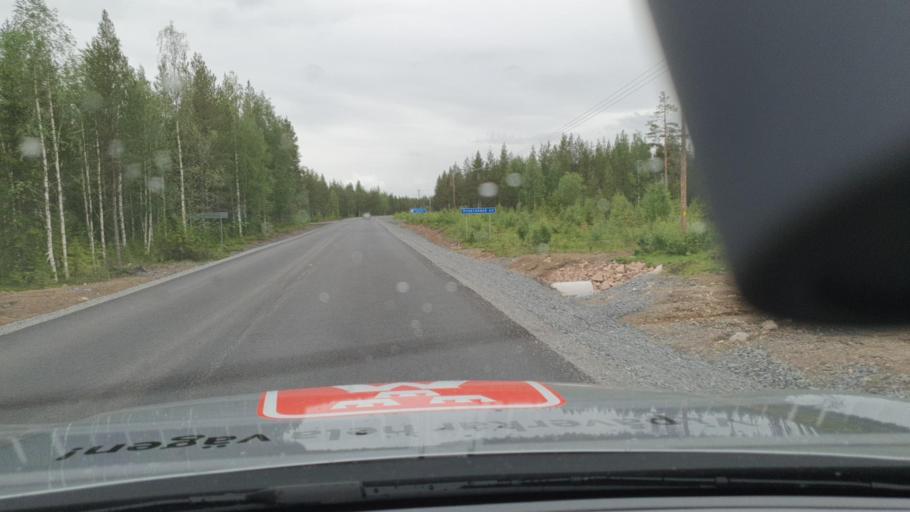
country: SE
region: Norrbotten
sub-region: Overkalix Kommun
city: OEverkalix
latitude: 66.6751
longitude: 23.2194
